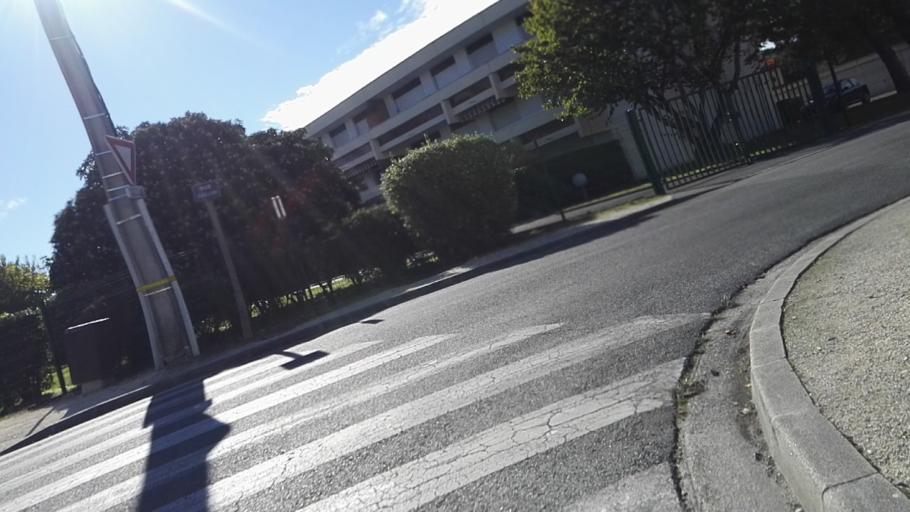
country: FR
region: Aquitaine
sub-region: Departement de la Gironde
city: Bruges
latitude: 44.8603
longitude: -0.6287
